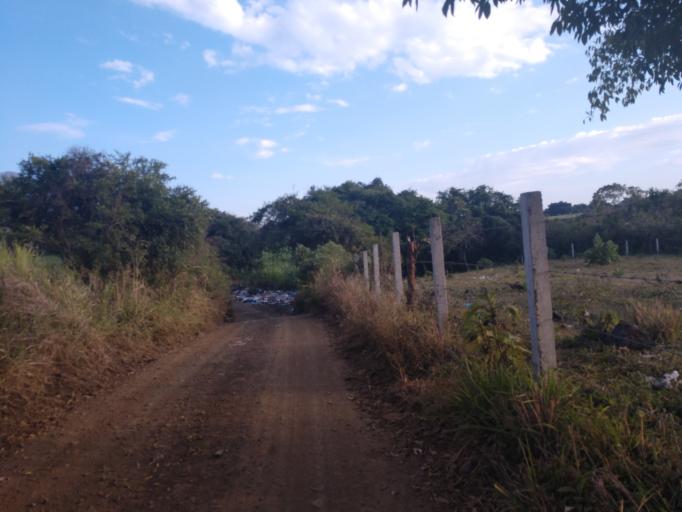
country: MX
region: Nayarit
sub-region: Tepic
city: La Corregidora
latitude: 21.4575
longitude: -104.7980
